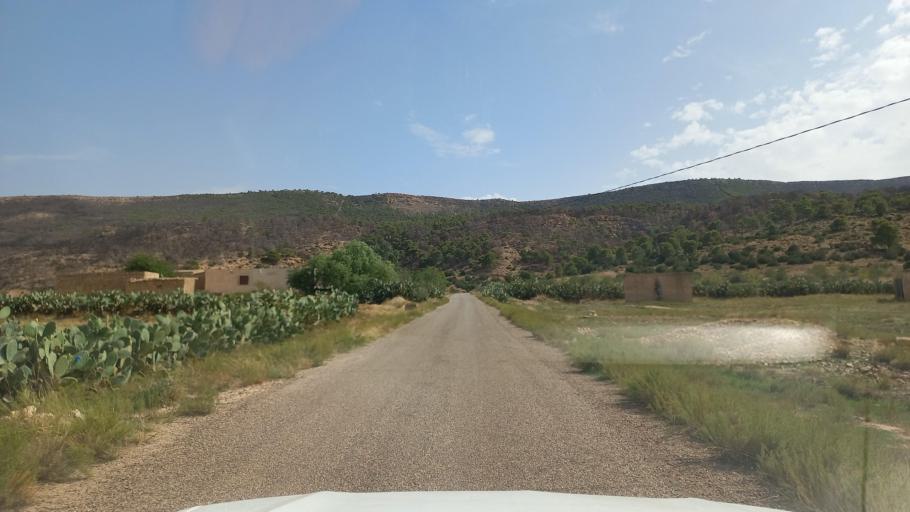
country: TN
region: Al Qasrayn
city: Kasserine
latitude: 35.3552
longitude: 8.8877
